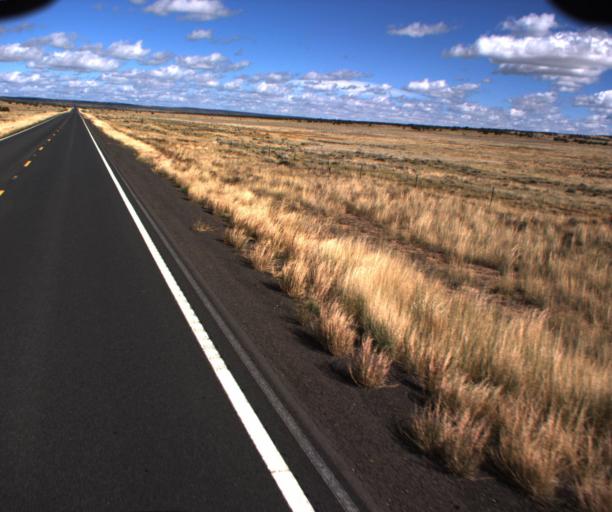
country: US
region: Arizona
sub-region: Apache County
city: Houck
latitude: 34.9796
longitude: -109.2270
